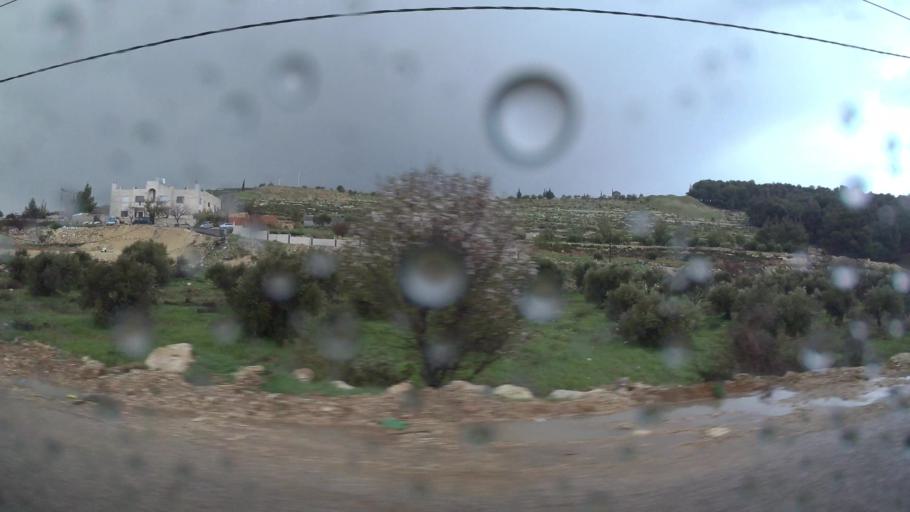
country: JO
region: Amman
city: Umm as Summaq
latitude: 31.8688
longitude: 35.8632
